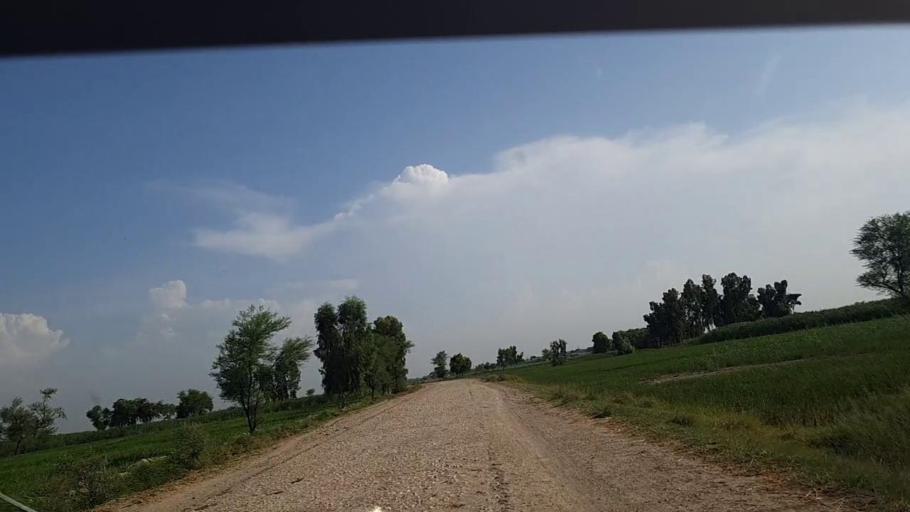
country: PK
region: Sindh
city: Khanpur
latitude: 27.8652
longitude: 69.3748
